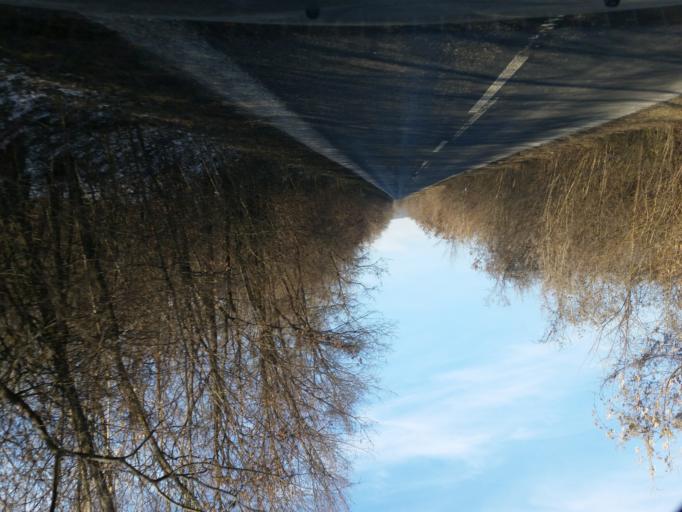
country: HU
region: Pest
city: Paty
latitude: 47.5321
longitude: 18.8400
